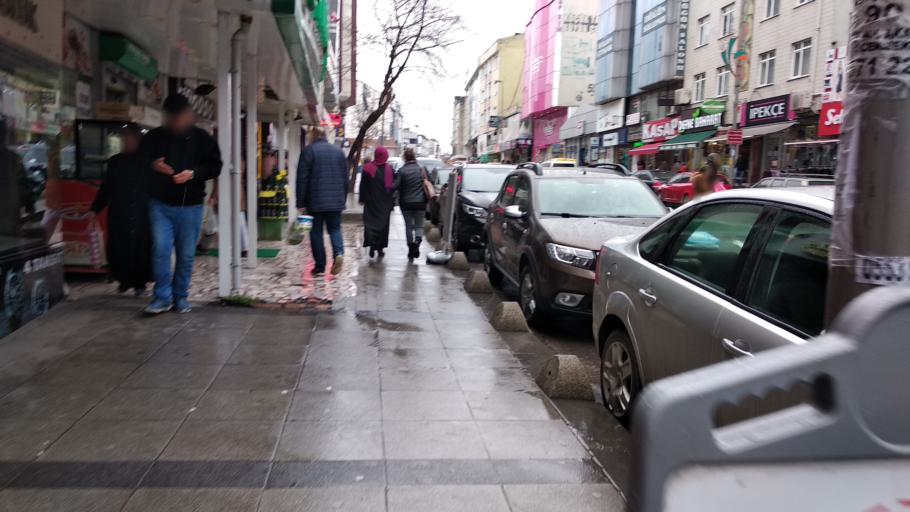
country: TR
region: Istanbul
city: Samandira
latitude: 41.0185
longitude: 29.1920
